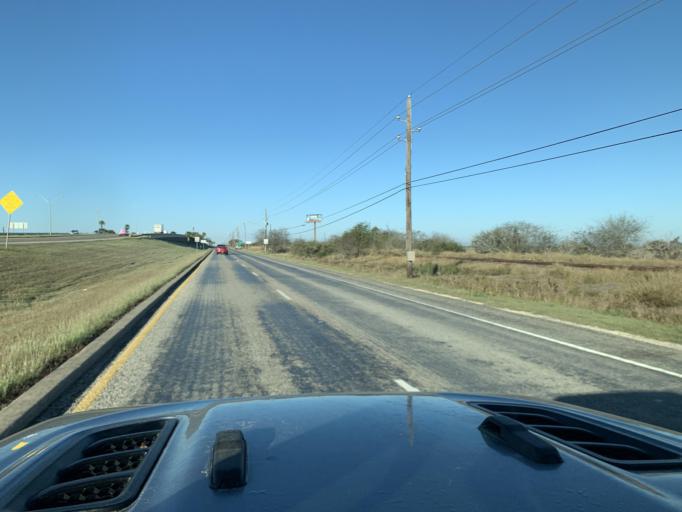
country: US
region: Texas
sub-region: Nueces County
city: Corpus Christi
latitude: 27.7853
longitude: -97.4987
